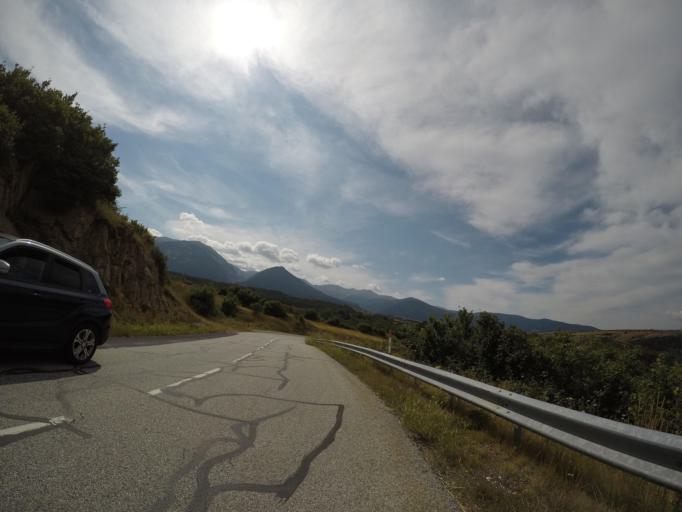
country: ES
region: Catalonia
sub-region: Provincia de Girona
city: Llivia
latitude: 42.4870
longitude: 2.0527
